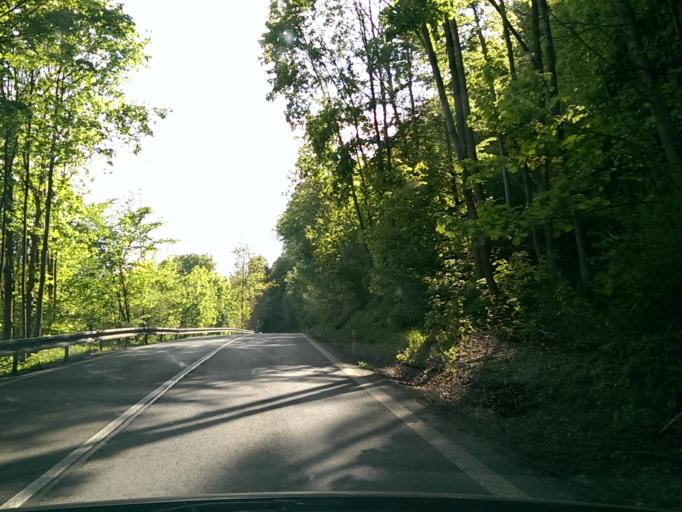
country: CZ
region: Liberecky
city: Mala Skala
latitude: 50.6248
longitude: 15.1776
